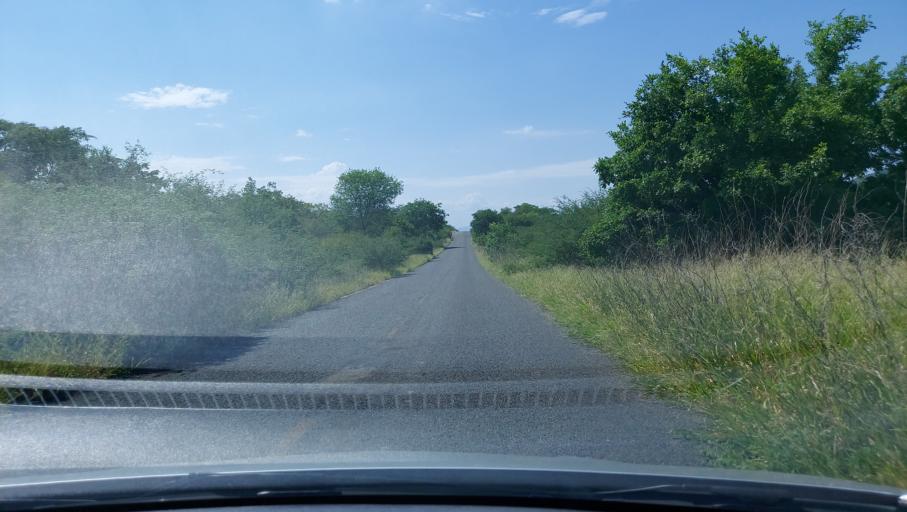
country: BR
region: Bahia
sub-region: Oliveira Dos Brejinhos
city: Beira Rio
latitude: -12.1675
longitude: -42.5471
